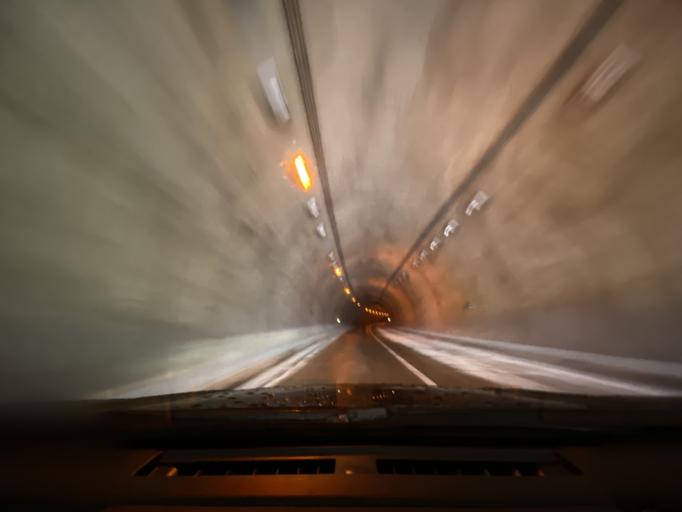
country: JP
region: Hokkaido
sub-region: Asahikawa-shi
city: Asahikawa
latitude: 43.8113
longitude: 142.2454
